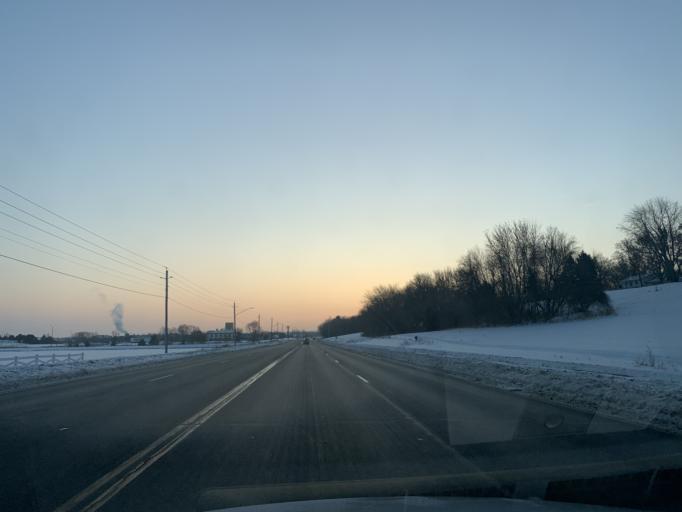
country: US
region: Minnesota
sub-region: Scott County
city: Shakopee
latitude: 44.7861
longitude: -93.4888
